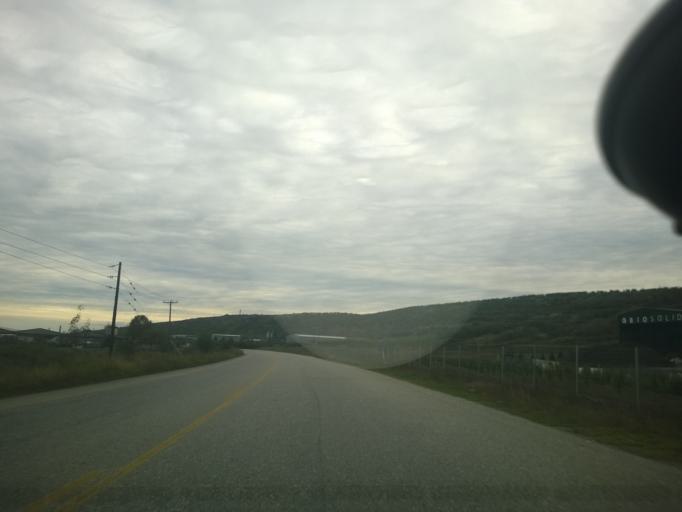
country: GR
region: Central Macedonia
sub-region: Nomos Pellis
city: Profitis Ilias
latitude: 40.8083
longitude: 22.1460
